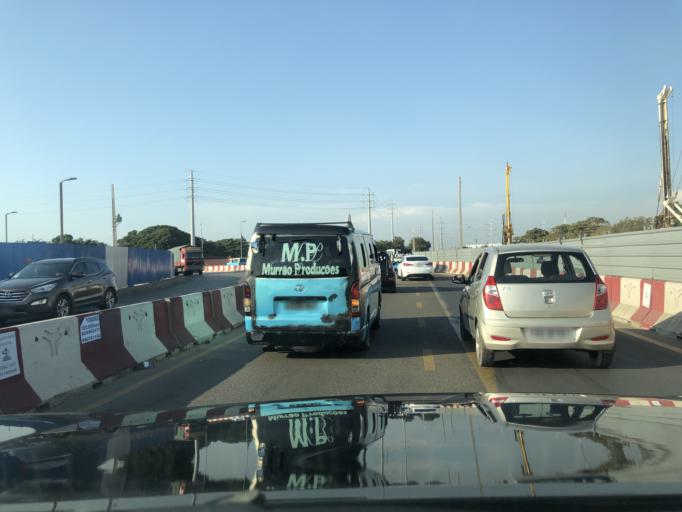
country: AO
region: Luanda
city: Luanda
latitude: -8.9090
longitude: 13.1798
